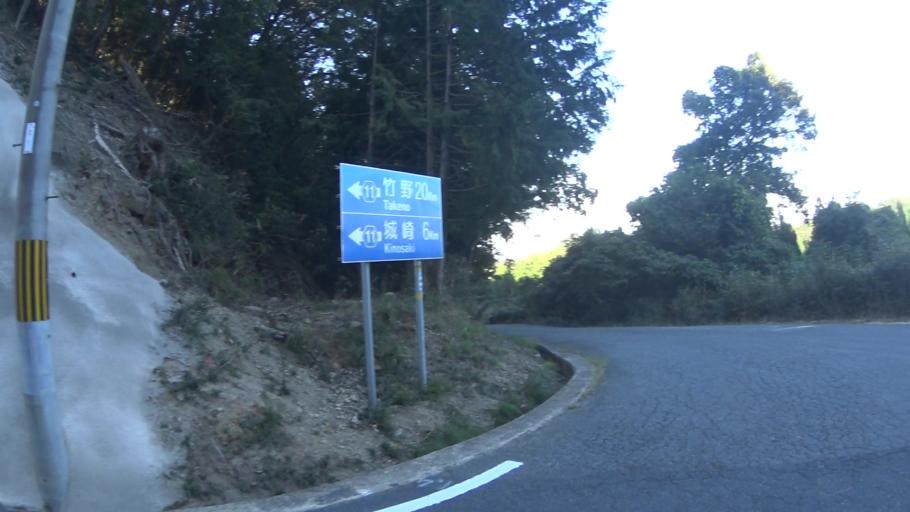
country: JP
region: Hyogo
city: Toyooka
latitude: 35.6178
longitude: 134.8728
